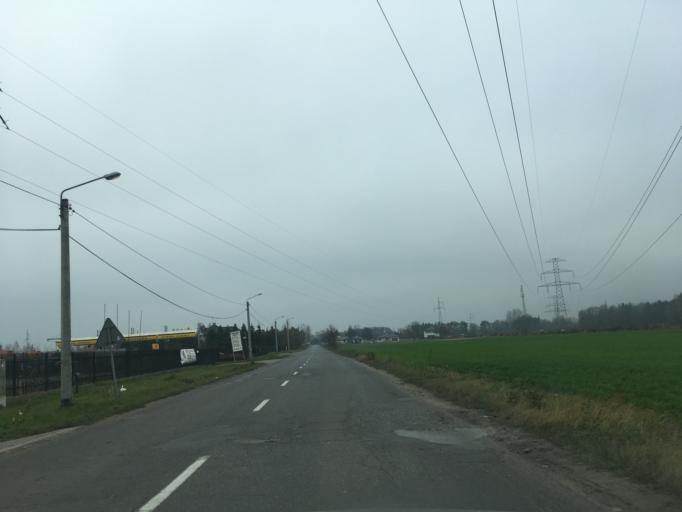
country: PL
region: Masovian Voivodeship
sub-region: Powiat piaseczynski
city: Lesznowola
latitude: 52.0801
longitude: 20.9674
